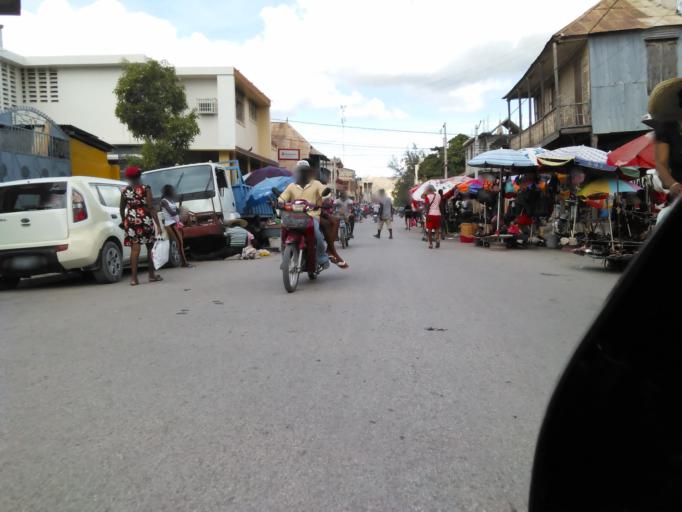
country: HT
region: Artibonite
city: Saint-Marc
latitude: 19.1073
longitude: -72.7000
